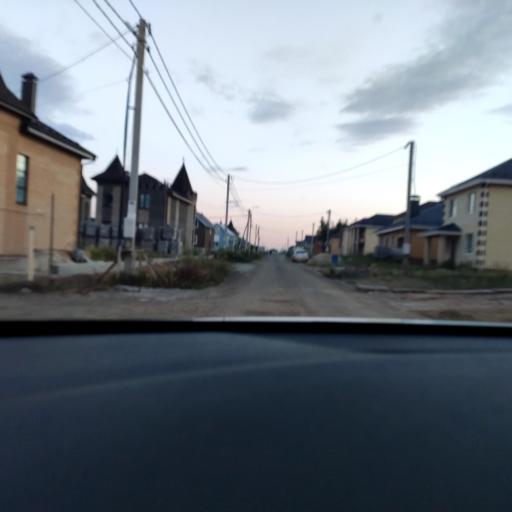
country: RU
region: Tatarstan
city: Stolbishchi
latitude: 55.7218
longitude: 49.2998
